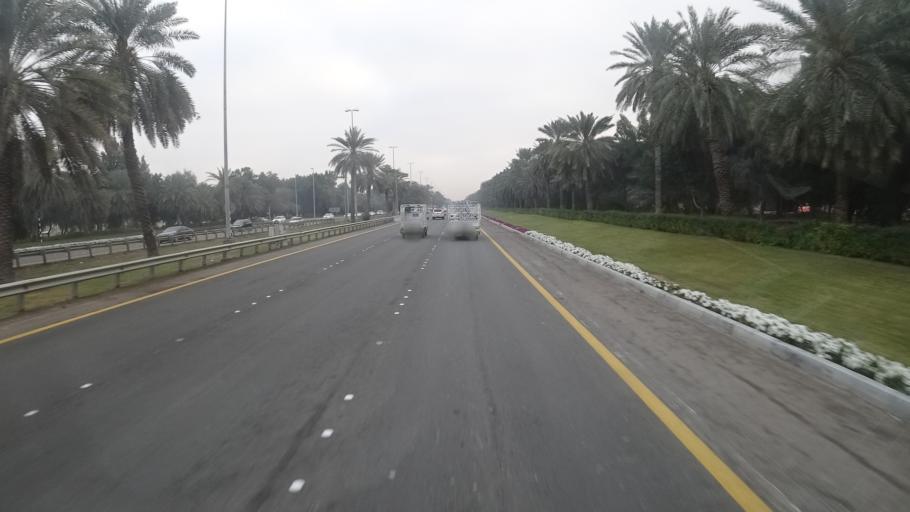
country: AE
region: Abu Dhabi
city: Abu Dhabi
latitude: 24.4034
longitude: 54.6042
